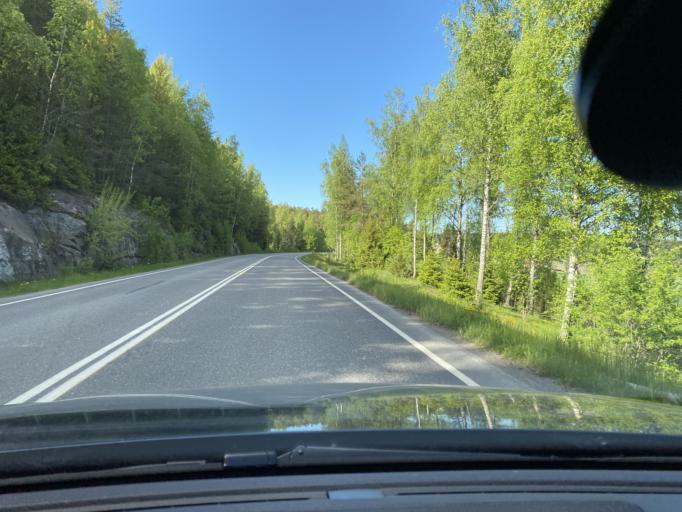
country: FI
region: Varsinais-Suomi
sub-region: Turku
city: Sauvo
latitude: 60.3602
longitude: 22.6715
